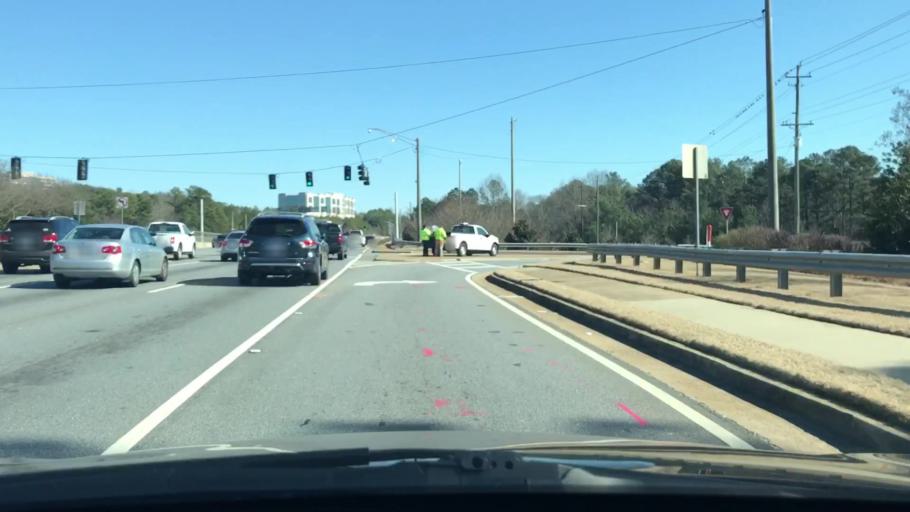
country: US
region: Georgia
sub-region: Fulton County
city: Alpharetta
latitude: 34.0683
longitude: -84.2736
